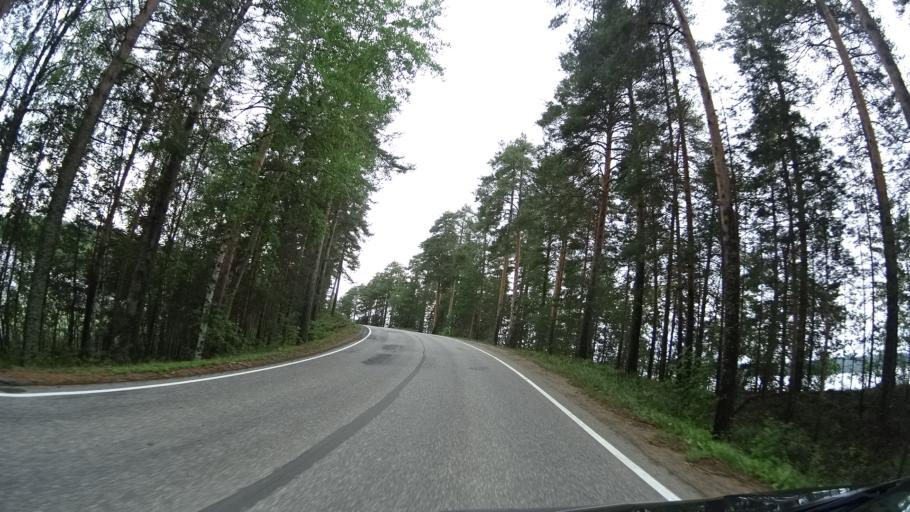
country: FI
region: Southern Savonia
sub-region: Savonlinna
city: Punkaharju
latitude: 61.7543
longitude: 29.4248
